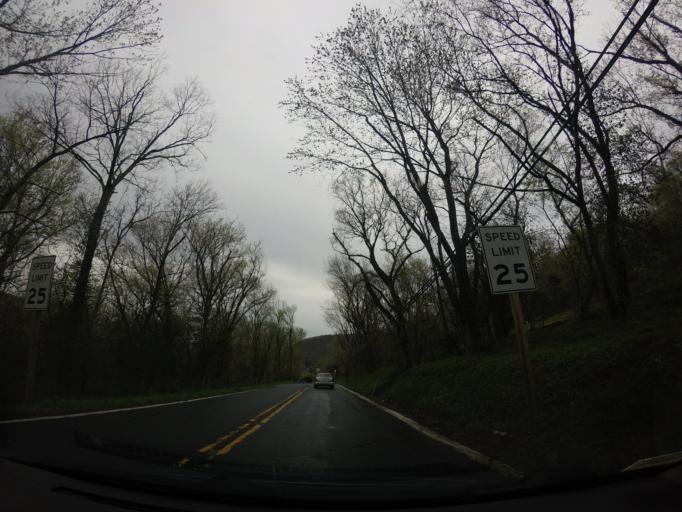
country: US
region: Maryland
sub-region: Frederick County
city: Brunswick
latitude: 39.3239
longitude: -77.6600
